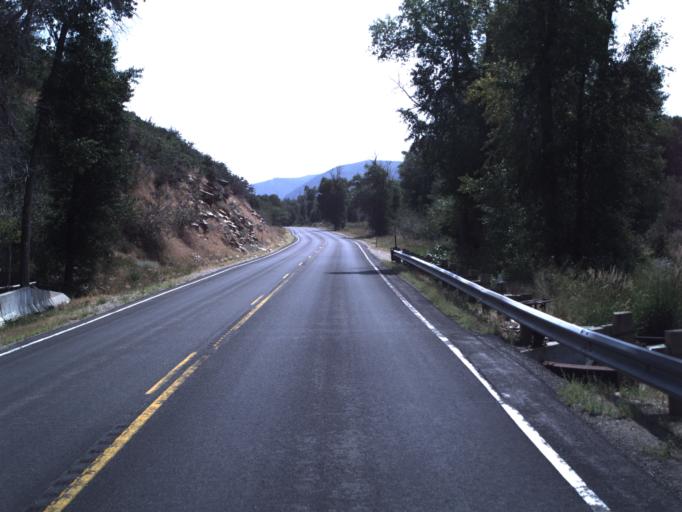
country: US
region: Utah
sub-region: Summit County
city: Francis
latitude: 40.5715
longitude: -111.2045
